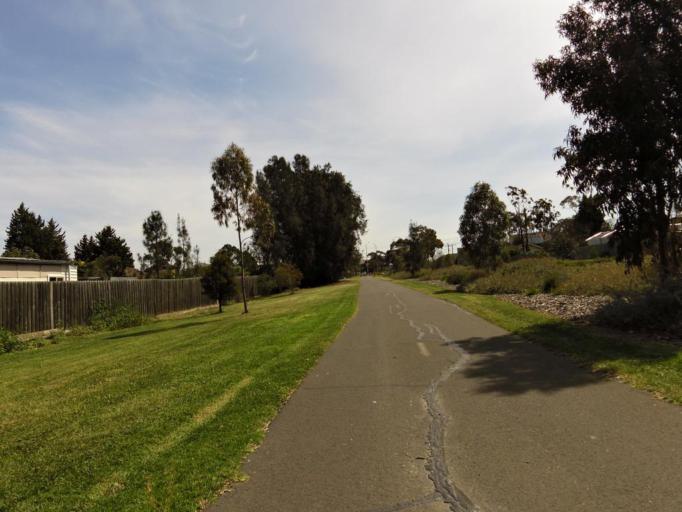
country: AU
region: Victoria
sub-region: Brimbank
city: Brooklyn
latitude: -37.8207
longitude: 144.8414
